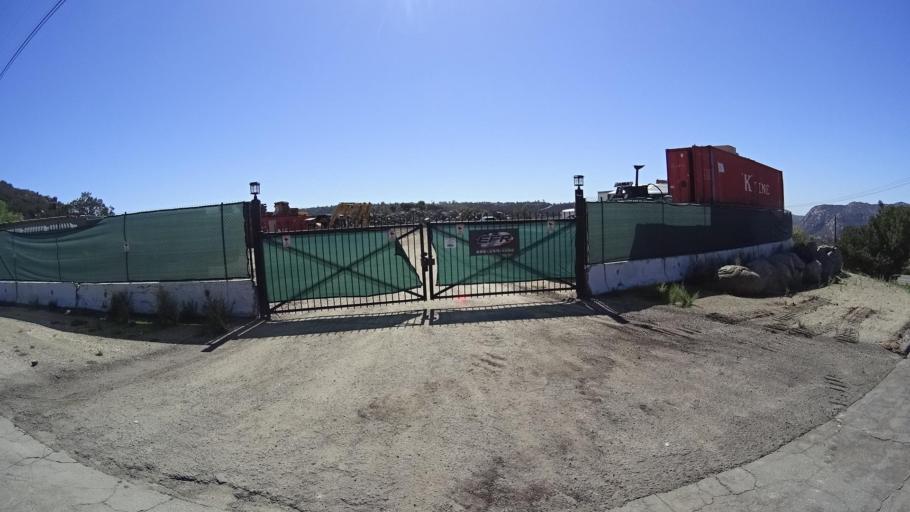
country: US
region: California
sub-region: San Diego County
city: Alpine
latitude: 32.8428
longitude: -116.7904
